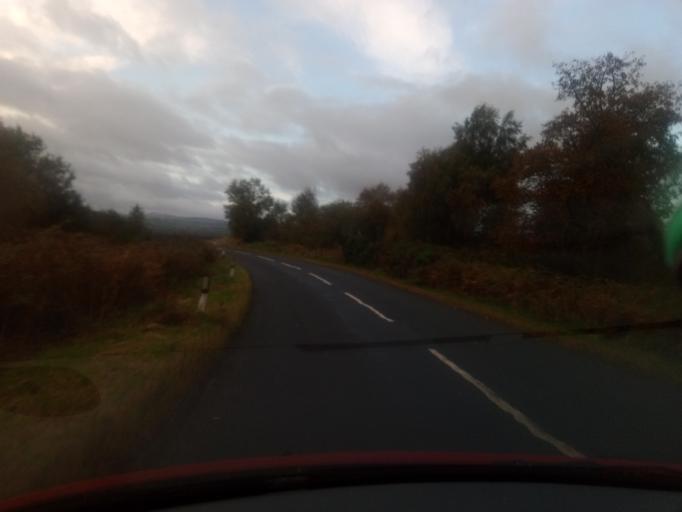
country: GB
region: Scotland
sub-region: The Scottish Borders
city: Jedburgh
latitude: 55.4334
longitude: -2.6075
